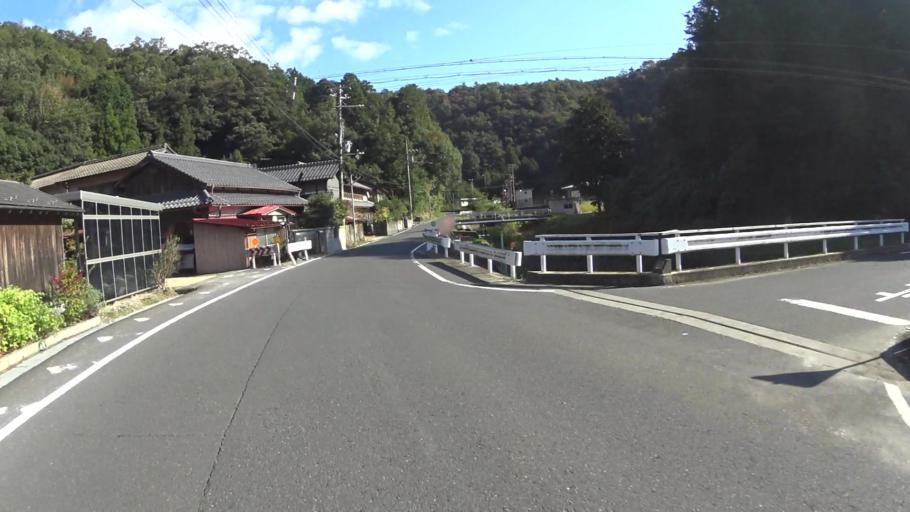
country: JP
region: Kyoto
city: Miyazu
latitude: 35.5768
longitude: 135.1601
